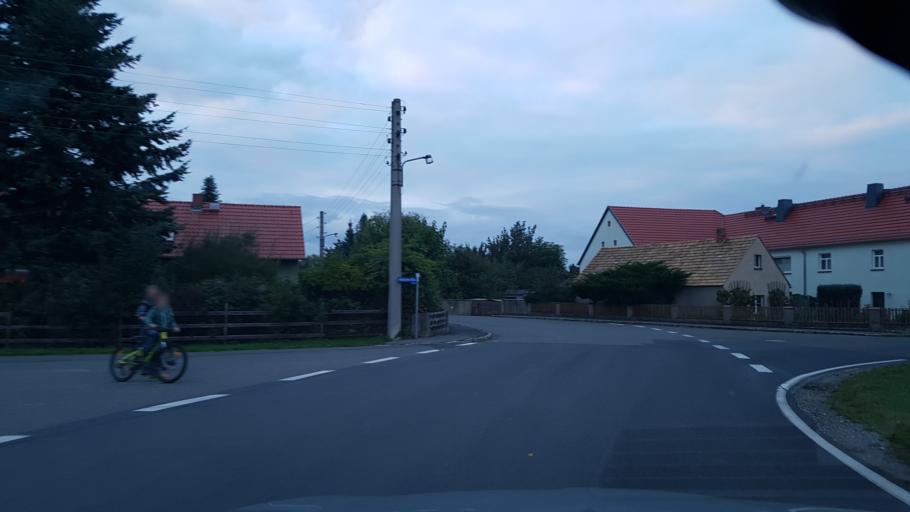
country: DE
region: Saxony
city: Grossenhain
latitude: 51.3253
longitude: 13.5595
